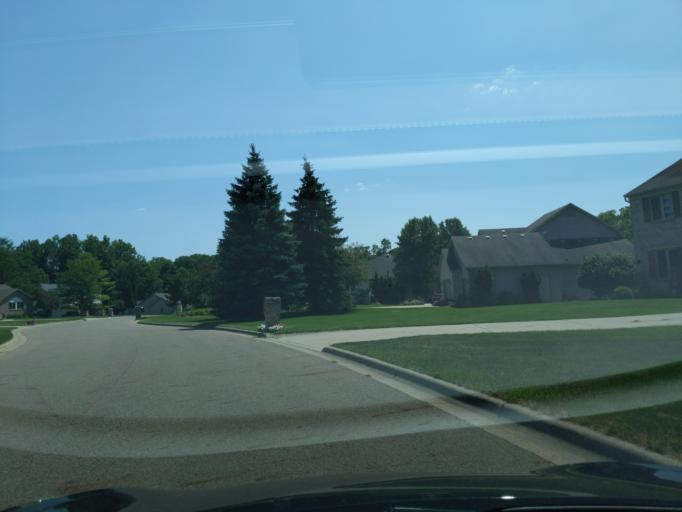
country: US
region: Michigan
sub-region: Ingham County
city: Edgemont Park
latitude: 42.7651
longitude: -84.6115
